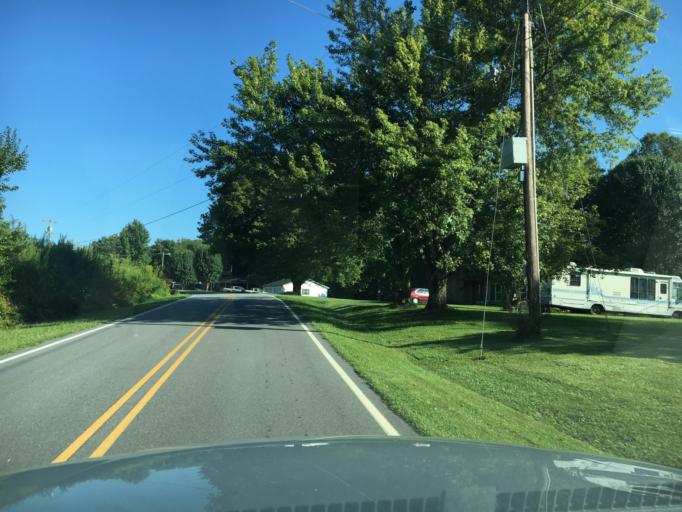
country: US
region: North Carolina
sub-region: McDowell County
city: West Marion
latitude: 35.6443
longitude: -82.0188
